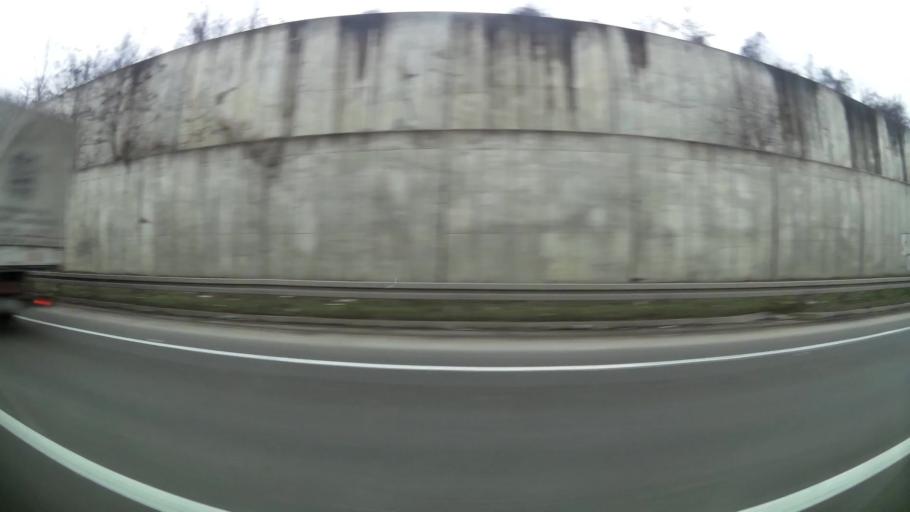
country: RS
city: Ostruznica
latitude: 44.7273
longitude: 20.3516
